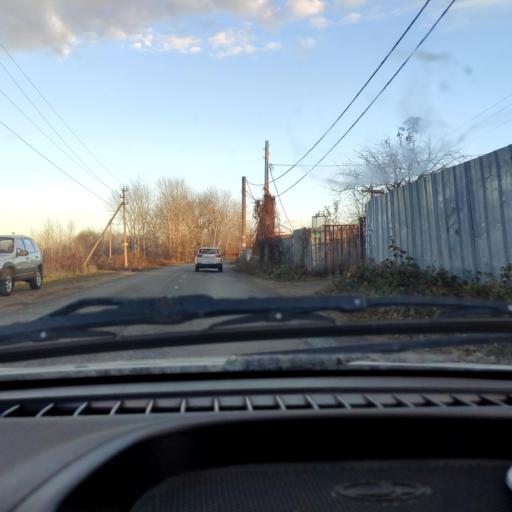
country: RU
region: Samara
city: Povolzhskiy
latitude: 53.4658
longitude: 49.6643
